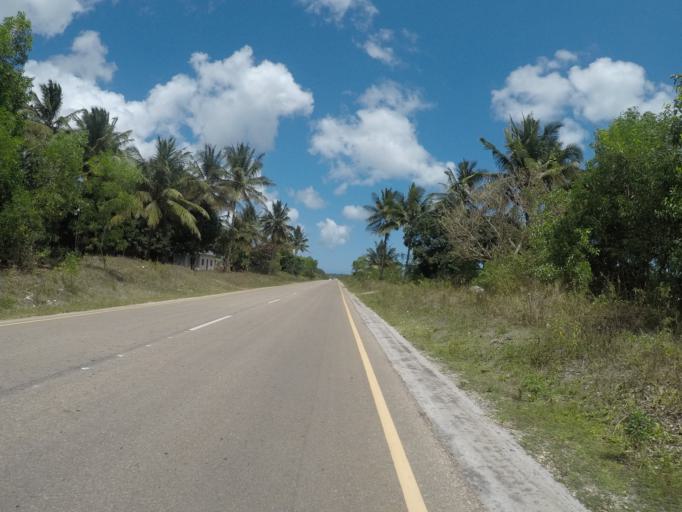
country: TZ
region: Zanzibar Central/South
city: Koani
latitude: -6.2680
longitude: 39.3618
